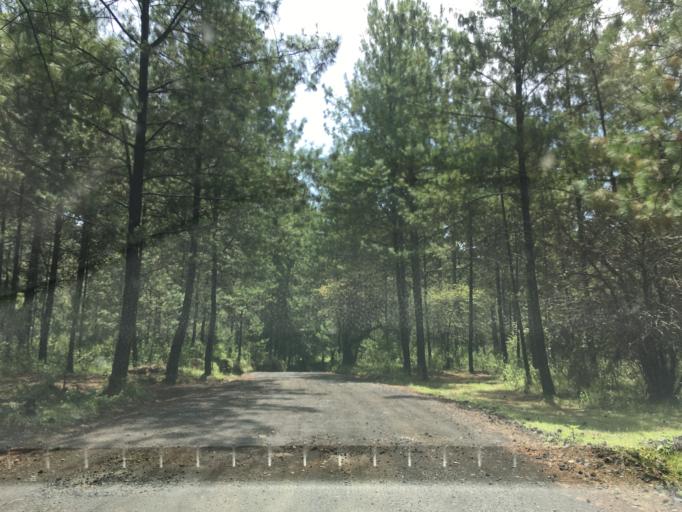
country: MX
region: Michoacan
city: Nuevo San Juan Parangaricutiro
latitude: 19.4578
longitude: -102.1900
